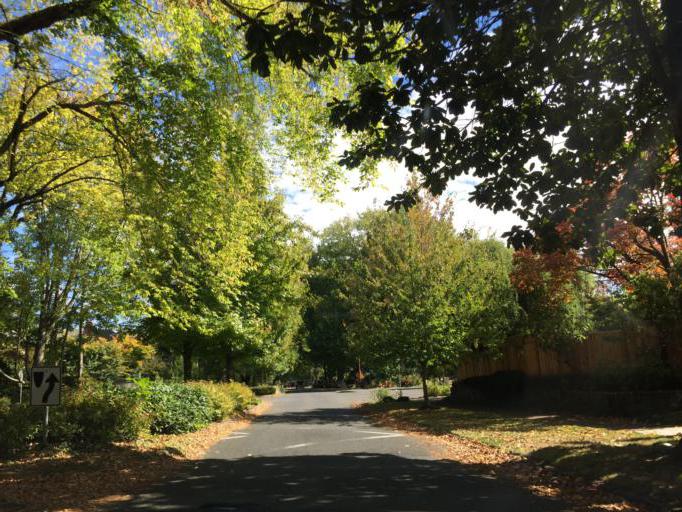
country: US
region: Oregon
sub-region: Multnomah County
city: Portland
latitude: 45.5308
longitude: -122.6255
